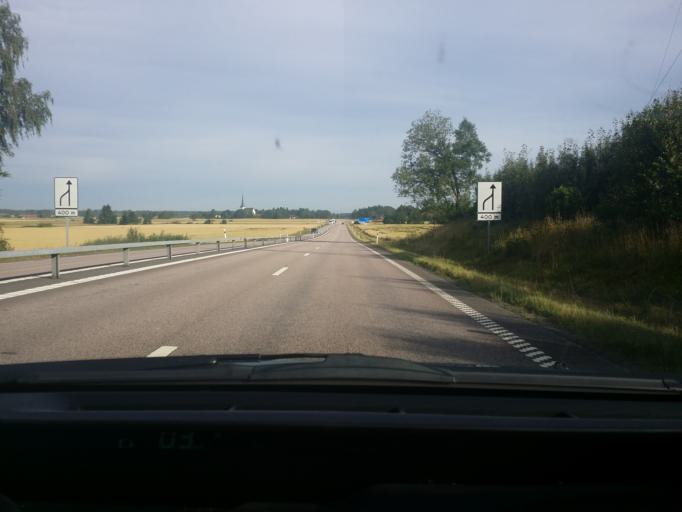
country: SE
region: Vaestmanland
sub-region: Vasteras
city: Hokasen
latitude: 59.7210
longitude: 16.5758
